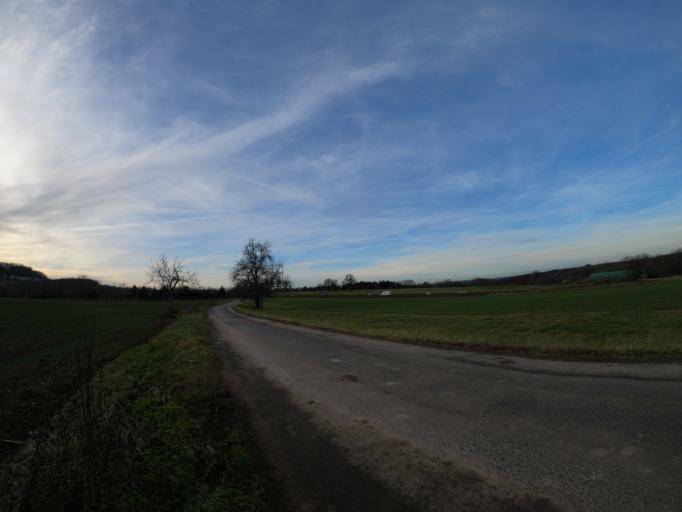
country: DE
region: Baden-Wuerttemberg
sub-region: Regierungsbezirk Stuttgart
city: Boll
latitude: 48.6400
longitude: 9.5937
